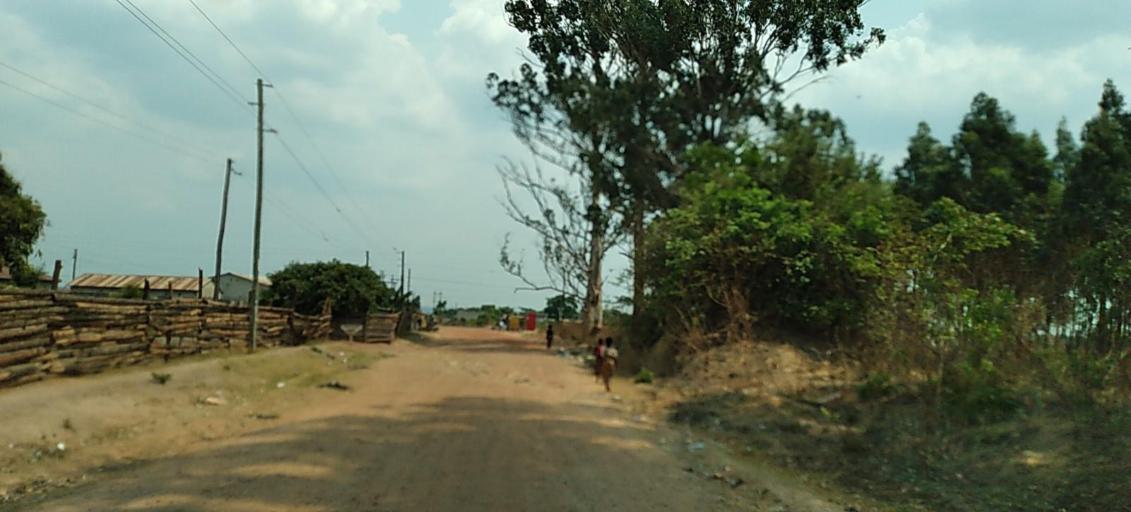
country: ZM
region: Copperbelt
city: Kalulushi
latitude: -12.8506
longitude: 28.0781
